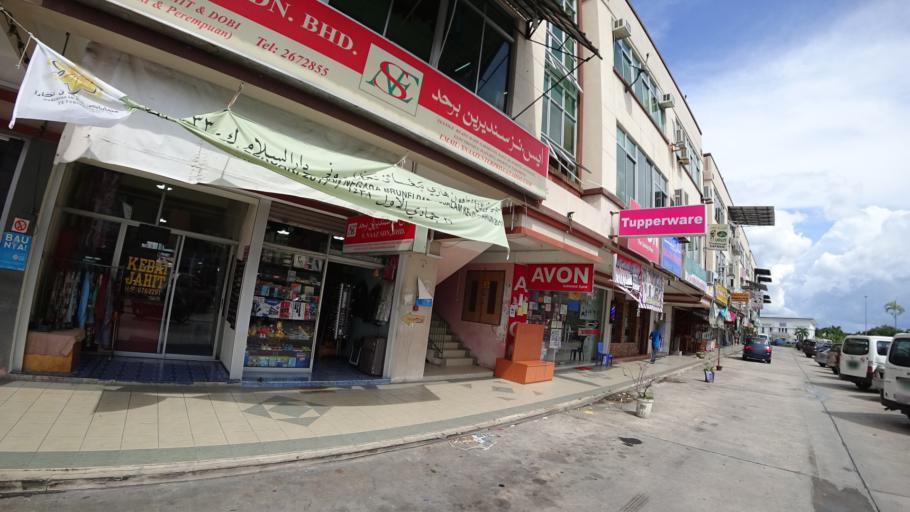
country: BN
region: Brunei and Muara
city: Bandar Seri Begawan
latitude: 4.8872
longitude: 114.8395
